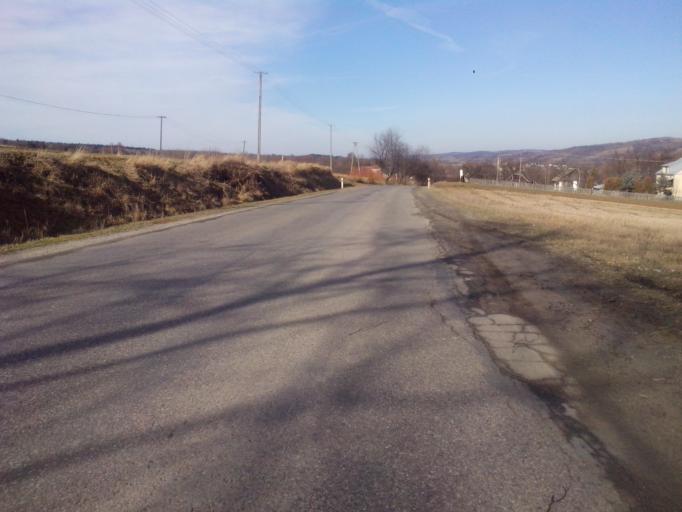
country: PL
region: Subcarpathian Voivodeship
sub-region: Powiat strzyzowski
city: Jawornik
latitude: 49.8195
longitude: 21.8349
